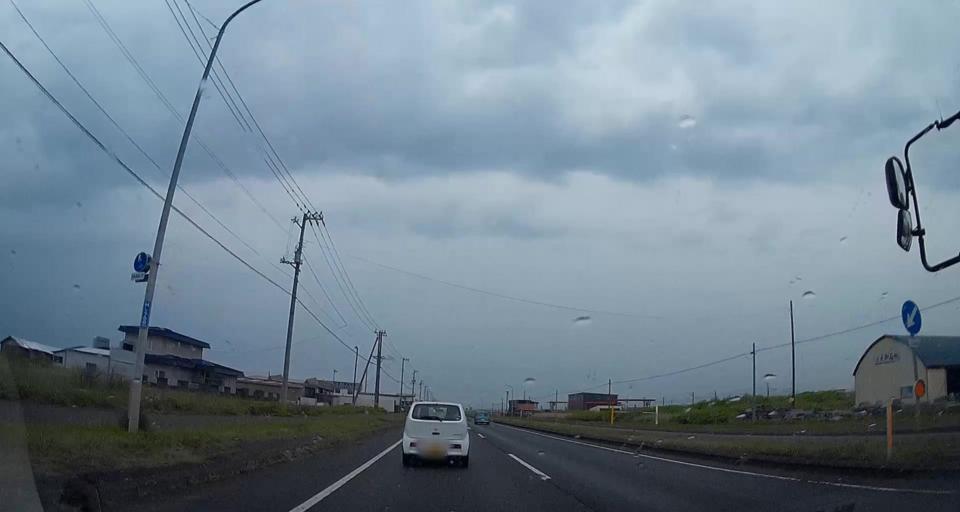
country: JP
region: Hokkaido
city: Tomakomai
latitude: 42.5982
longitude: 141.4772
